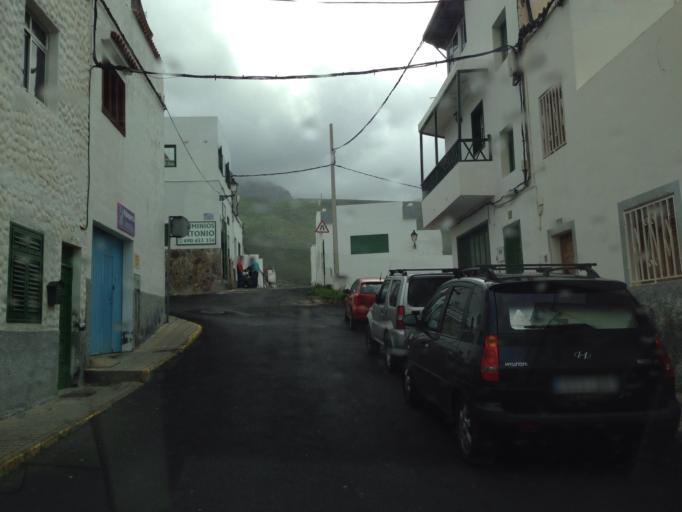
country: ES
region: Canary Islands
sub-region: Provincia de Las Palmas
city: Agaete
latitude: 28.0995
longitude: -15.6956
